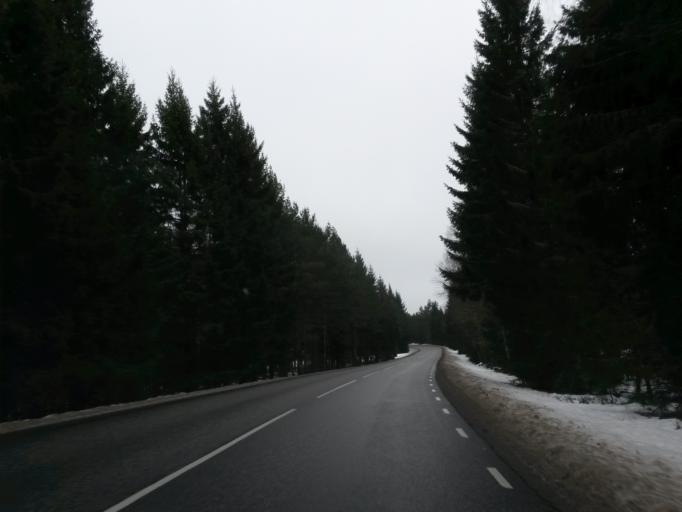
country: SE
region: Vaestra Goetaland
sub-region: Vargarda Kommun
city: Vargarda
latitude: 57.9856
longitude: 12.8464
